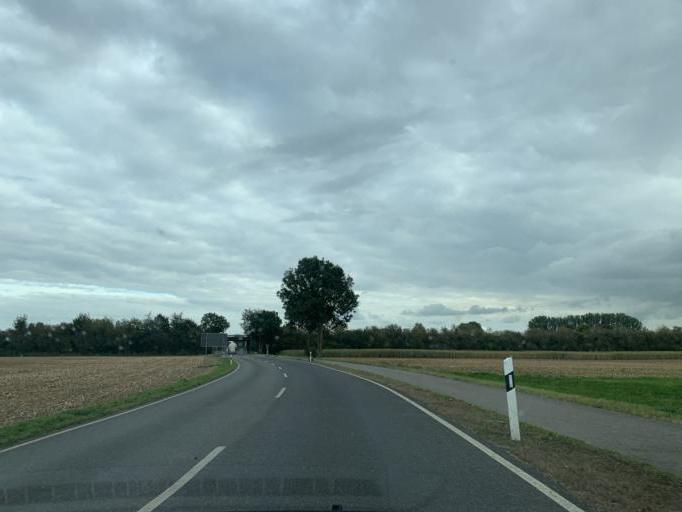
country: DE
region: North Rhine-Westphalia
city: Huckelhoven
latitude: 51.0545
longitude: 6.1774
